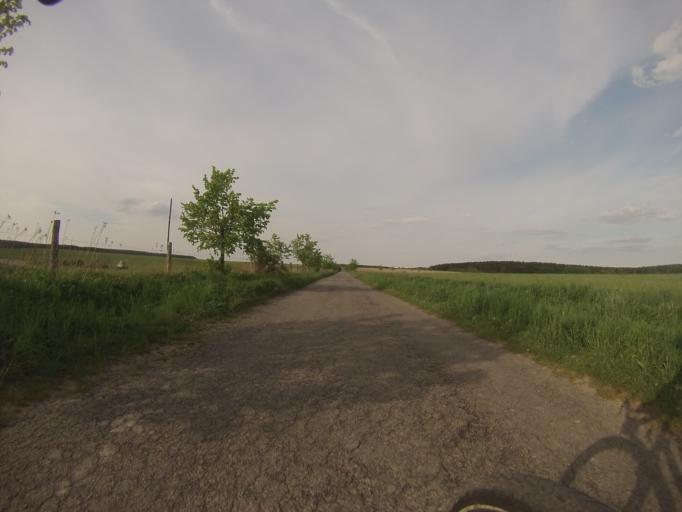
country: CZ
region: Olomoucky
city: Protivanov
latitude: 49.4451
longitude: 16.8594
